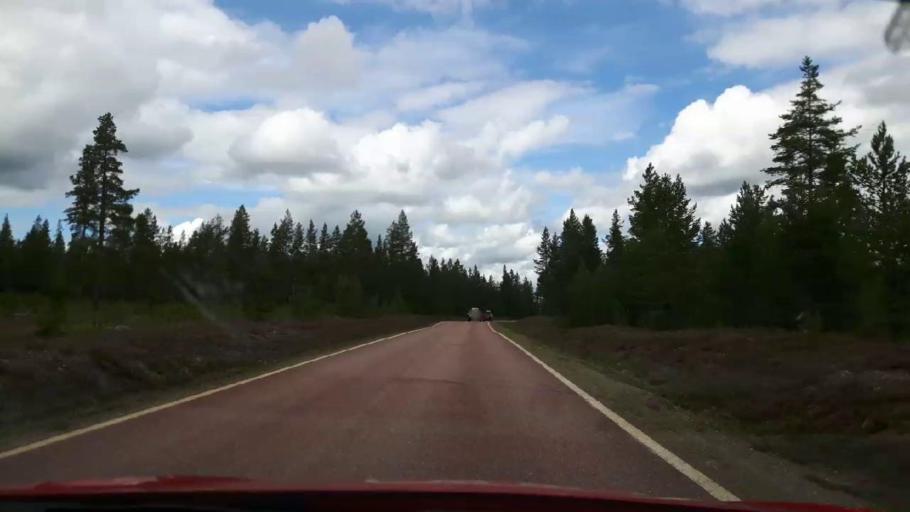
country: NO
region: Hedmark
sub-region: Trysil
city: Innbygda
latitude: 61.8560
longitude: 12.9478
